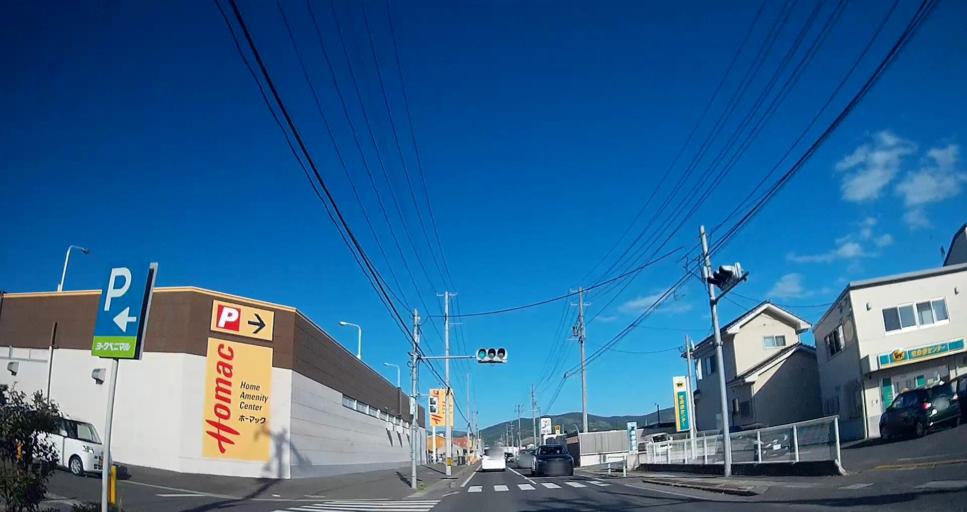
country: JP
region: Miyagi
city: Ishinomaki
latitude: 38.4185
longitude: 141.3391
